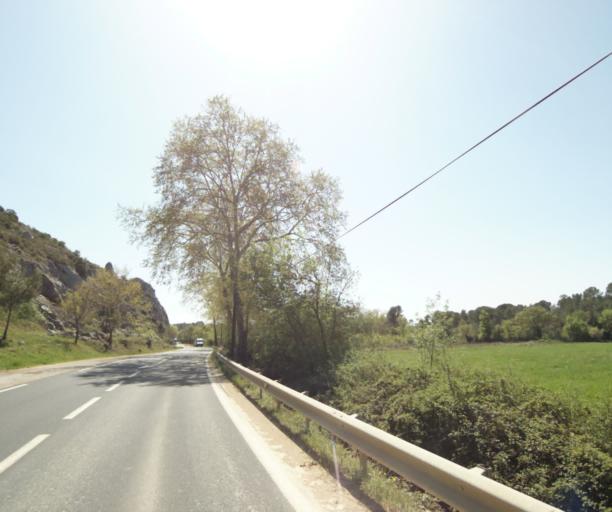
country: FR
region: Languedoc-Roussillon
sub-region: Departement de l'Herault
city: Prades-le-Lez
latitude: 43.7081
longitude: 3.8679
